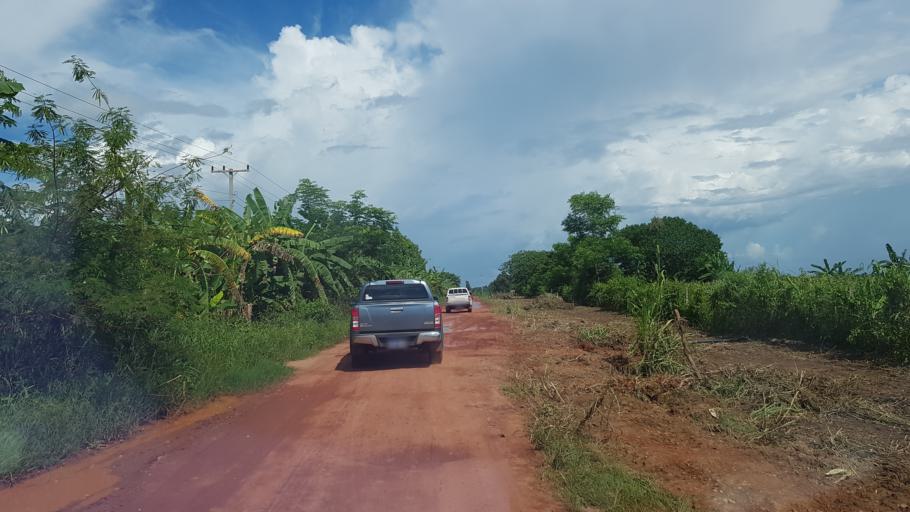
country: LA
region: Vientiane
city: Vientiane
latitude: 18.2250
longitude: 102.5661
